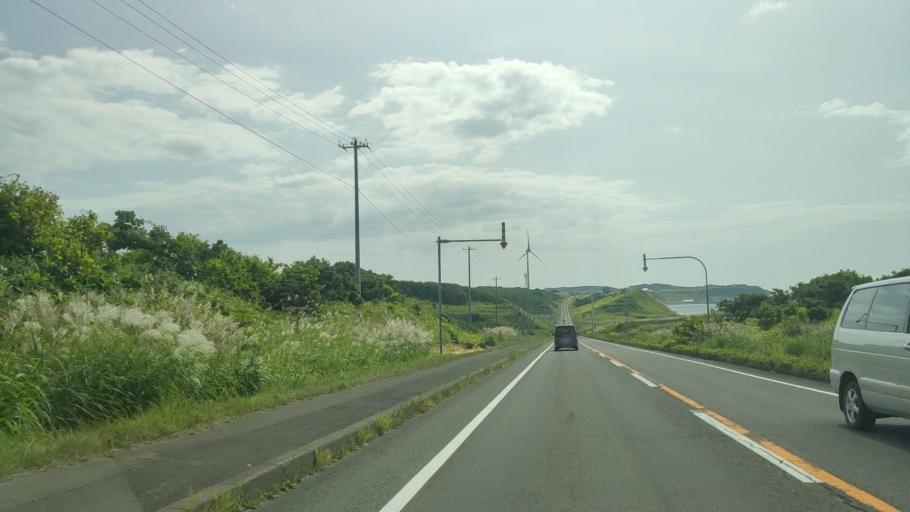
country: JP
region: Hokkaido
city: Rumoi
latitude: 44.3259
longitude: 141.6751
